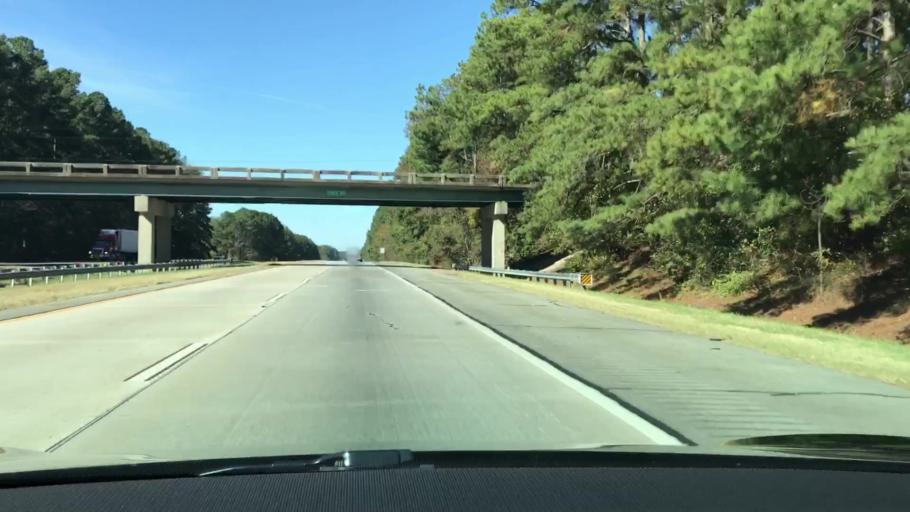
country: US
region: Georgia
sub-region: Greene County
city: Union Point
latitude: 33.5404
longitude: -83.0085
